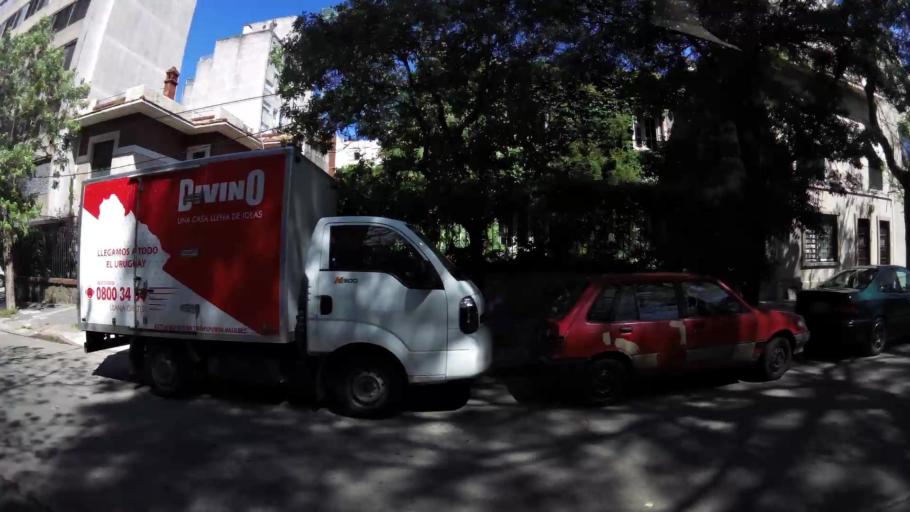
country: UY
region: Montevideo
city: Montevideo
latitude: -34.9100
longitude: -56.1496
